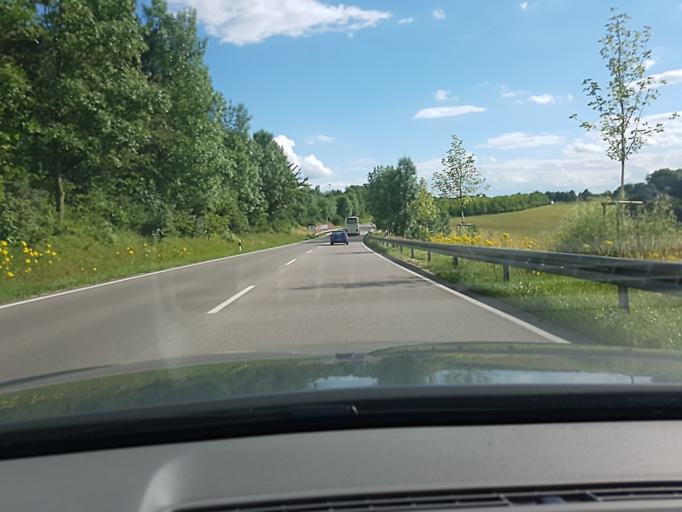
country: DE
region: Baden-Wuerttemberg
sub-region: Tuebingen Region
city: Ulm
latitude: 48.4314
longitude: 10.0106
